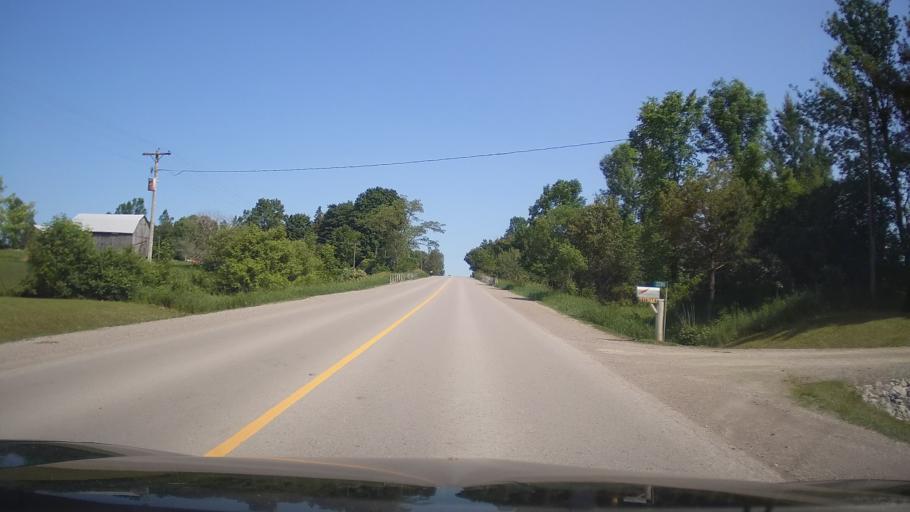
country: CA
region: Ontario
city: Orillia
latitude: 44.6339
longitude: -79.1006
